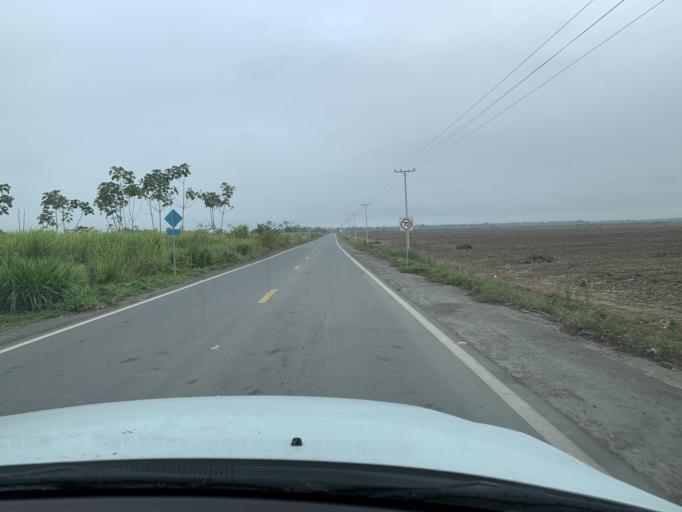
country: EC
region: Guayas
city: Coronel Marcelino Mariduena
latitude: -2.3053
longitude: -79.5025
